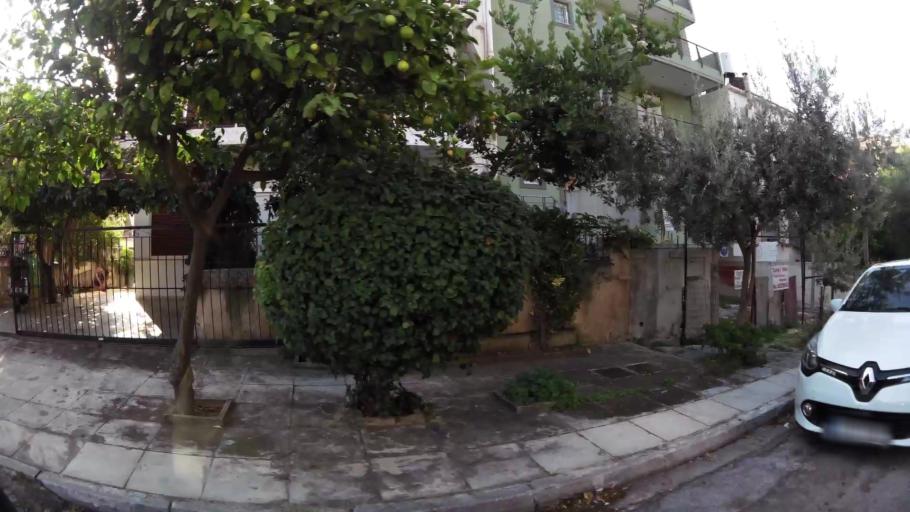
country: GR
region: Attica
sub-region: Nomarchia Athinas
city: Ilioupoli
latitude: 37.9340
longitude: 23.7531
